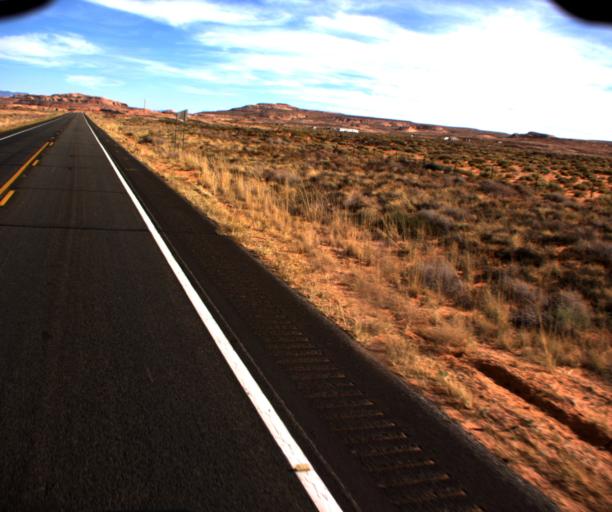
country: US
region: Arizona
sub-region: Apache County
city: Many Farms
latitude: 36.9319
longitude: -109.6269
